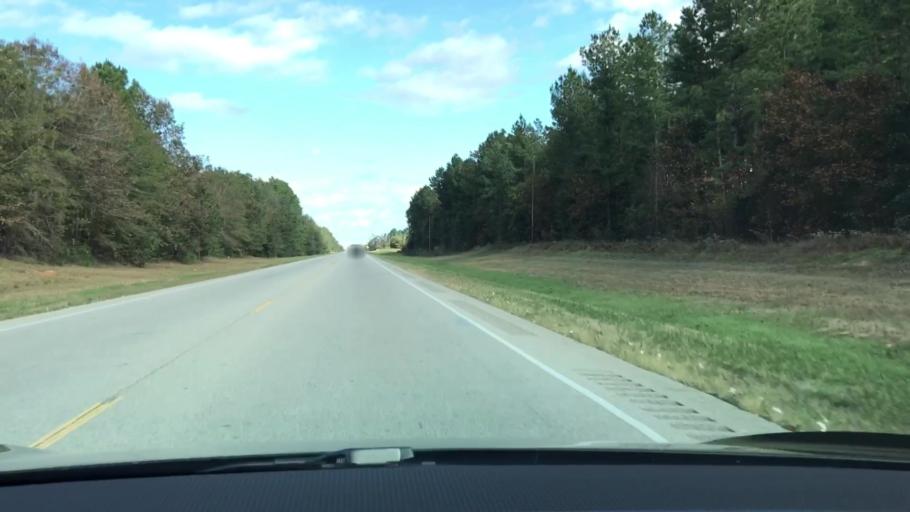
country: US
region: Georgia
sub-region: Jefferson County
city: Wadley
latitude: 32.9145
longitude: -82.3985
